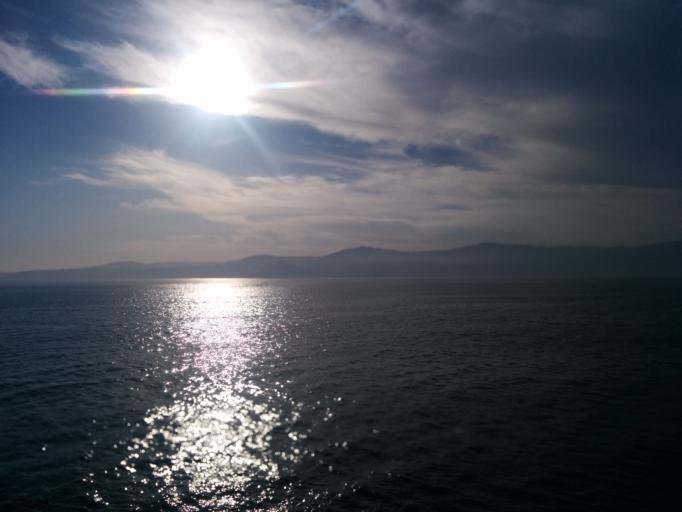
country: MA
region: Tanger-Tetouan
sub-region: Tanger-Assilah
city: Tangier
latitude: 35.8220
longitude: -5.7765
